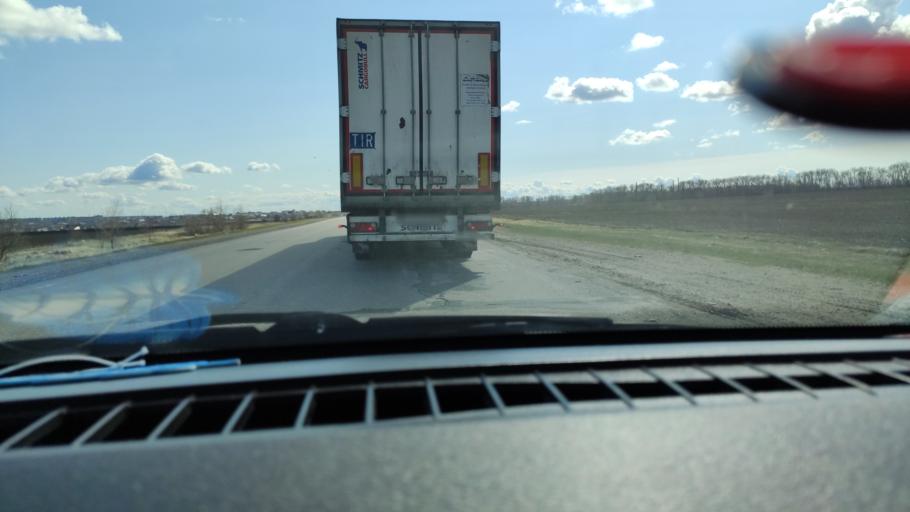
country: RU
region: Samara
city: Varlamovo
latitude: 53.1183
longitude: 48.3369
